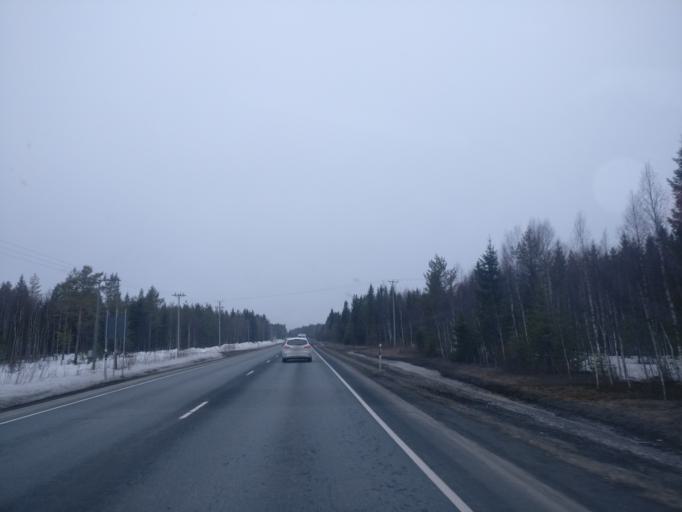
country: FI
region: Lapland
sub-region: Kemi-Tornio
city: Simo
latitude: 65.6718
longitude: 24.9142
